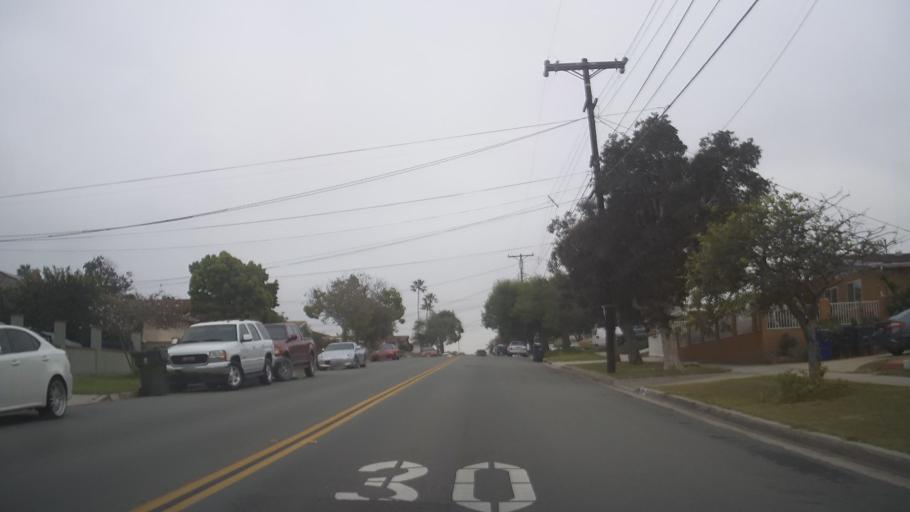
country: US
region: California
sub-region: San Diego County
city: Bonita
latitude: 32.6264
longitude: -117.0493
